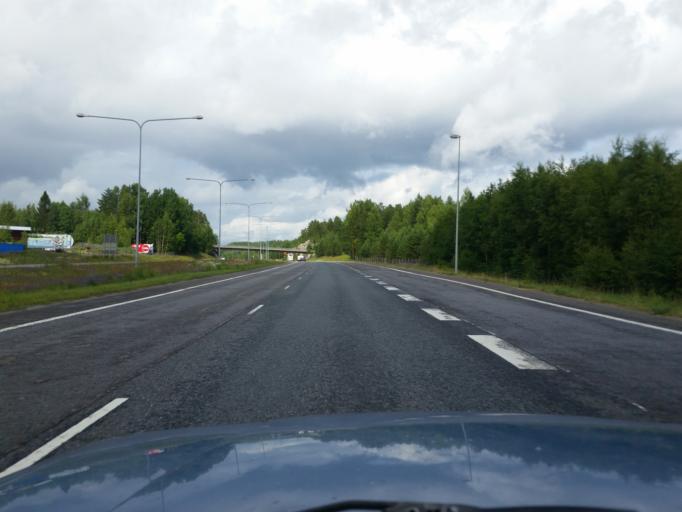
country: FI
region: Paijanne Tavastia
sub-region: Lahti
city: Heinola
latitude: 61.2378
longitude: 26.0465
